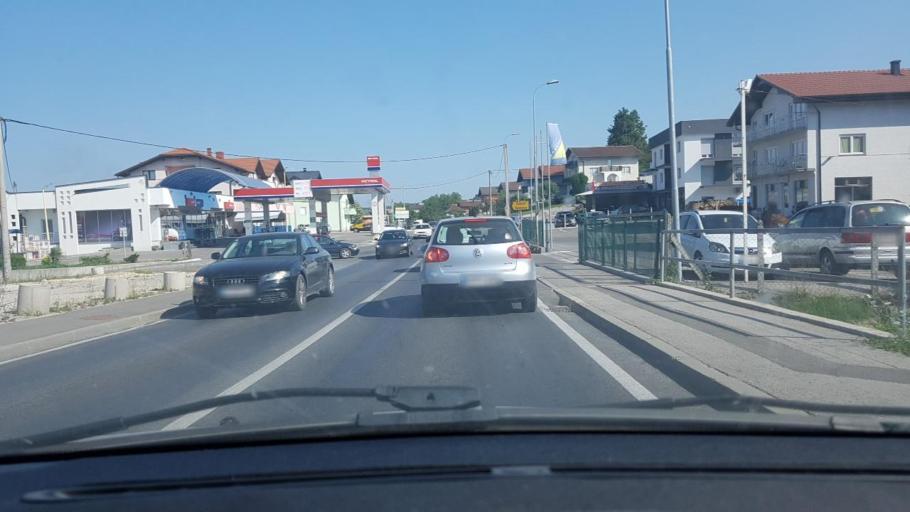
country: BA
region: Federation of Bosnia and Herzegovina
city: Cazin
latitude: 44.9690
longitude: 15.8991
